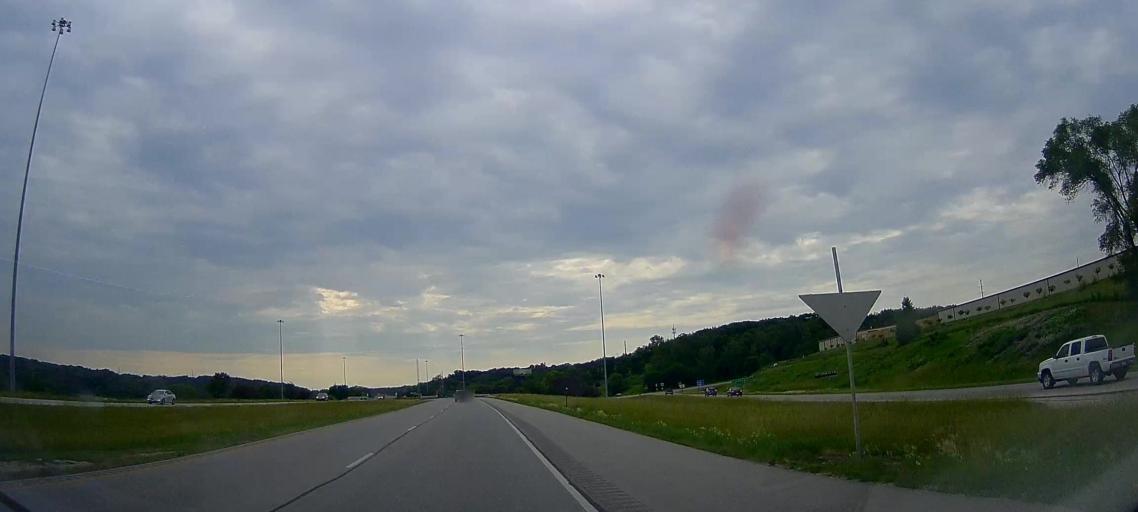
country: US
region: Iowa
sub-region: Pottawattamie County
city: Carter Lake
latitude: 41.3471
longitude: -95.9796
